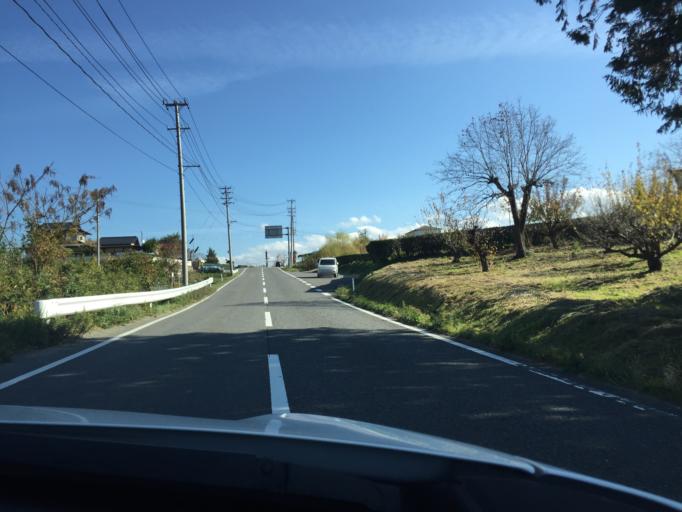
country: JP
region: Fukushima
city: Koriyama
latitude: 37.3834
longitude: 140.4130
